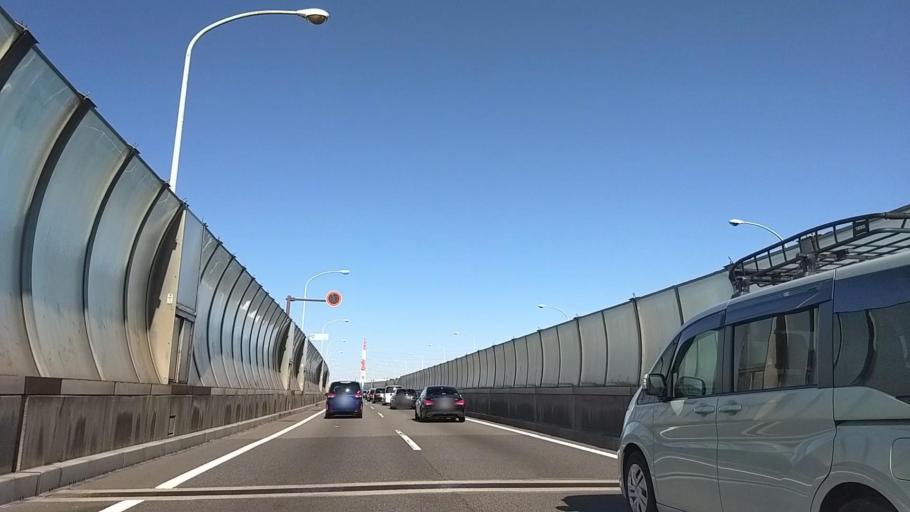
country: JP
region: Kanagawa
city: Minami-rinkan
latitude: 35.4993
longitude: 139.4924
